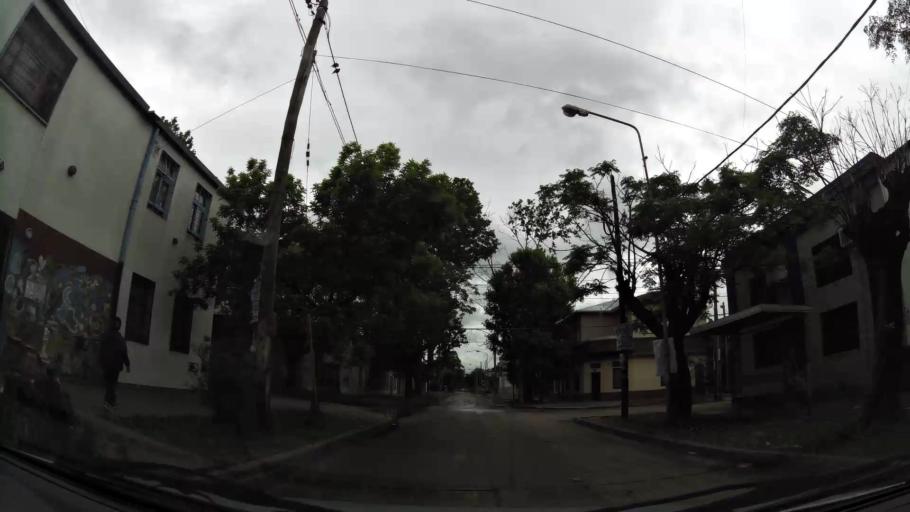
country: AR
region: Buenos Aires
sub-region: Partido de Lanus
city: Lanus
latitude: -34.7279
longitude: -58.3831
